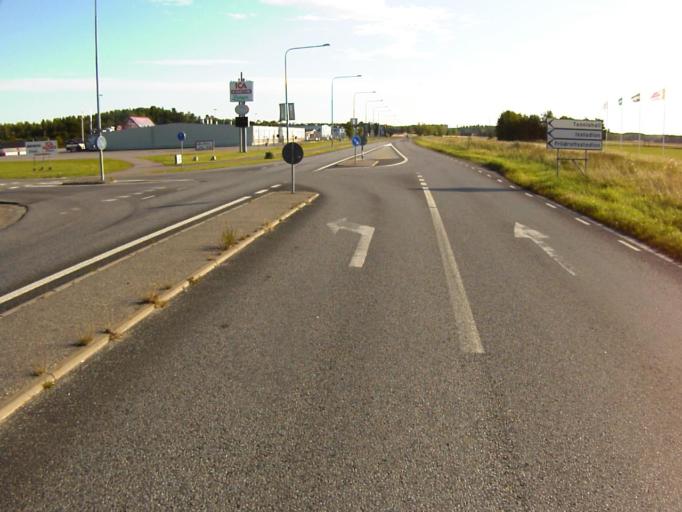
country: SE
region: Soedermanland
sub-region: Eskilstuna Kommun
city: Eskilstuna
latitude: 59.3704
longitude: 16.5522
